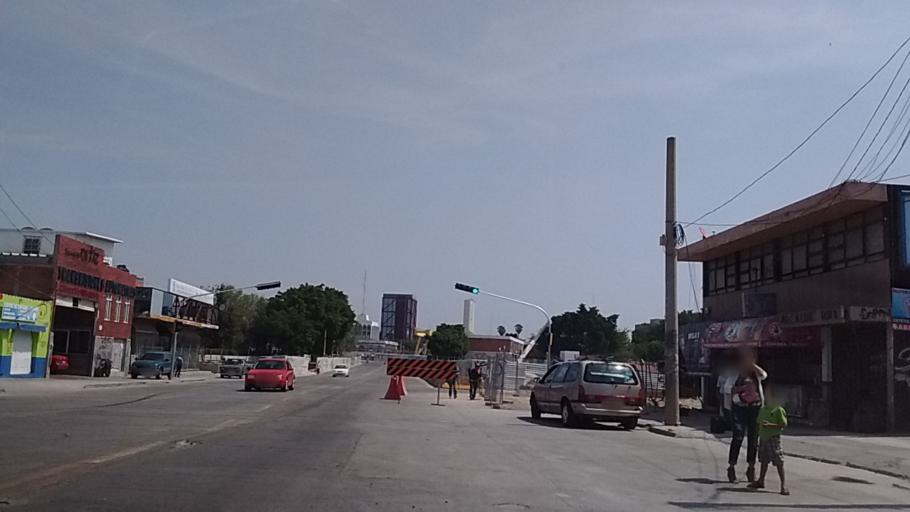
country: MX
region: Jalisco
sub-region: Zapopan
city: Zapopan
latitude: 20.6918
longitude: -103.3480
